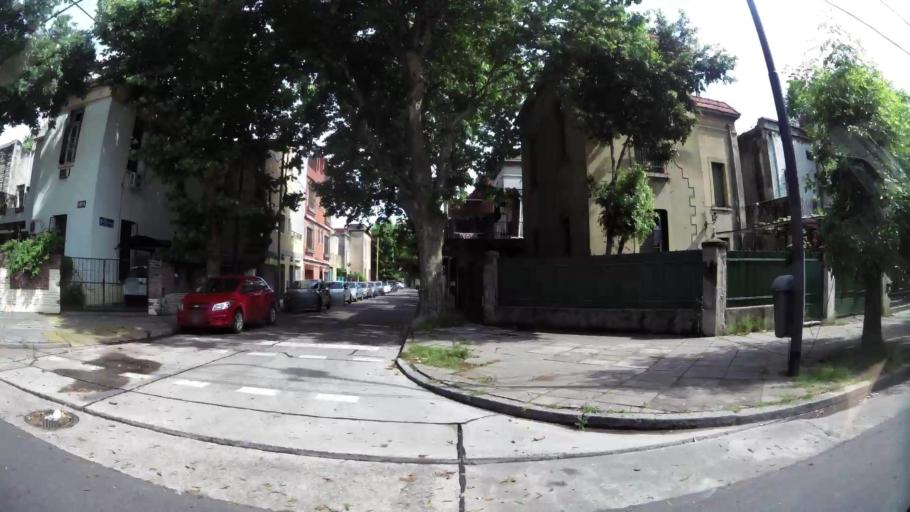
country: AR
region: Buenos Aires
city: San Justo
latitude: -34.6458
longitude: -58.5239
